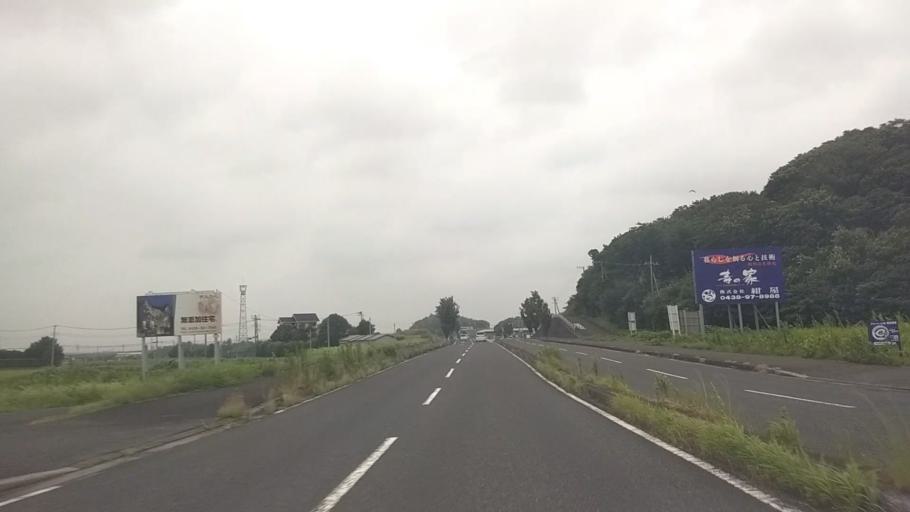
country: JP
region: Chiba
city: Kisarazu
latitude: 35.3832
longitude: 139.9677
